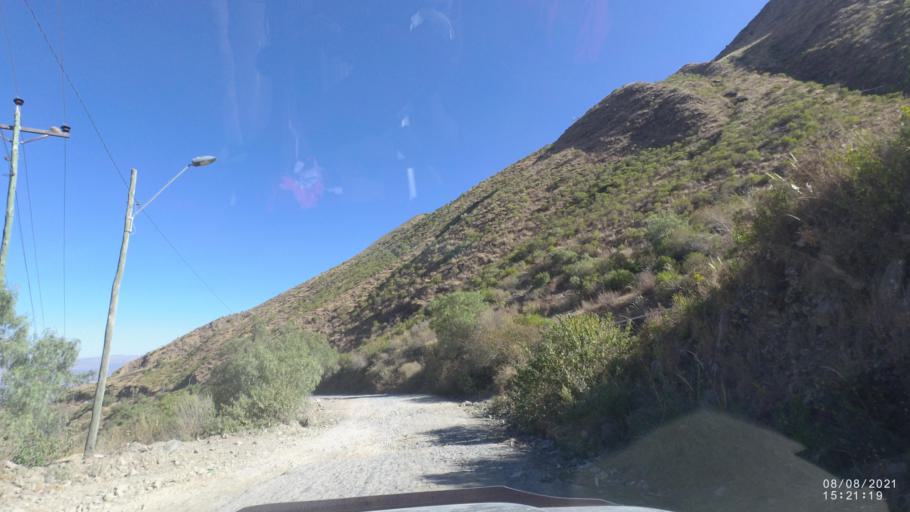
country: BO
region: Cochabamba
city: Cochabamba
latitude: -17.3016
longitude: -66.2955
